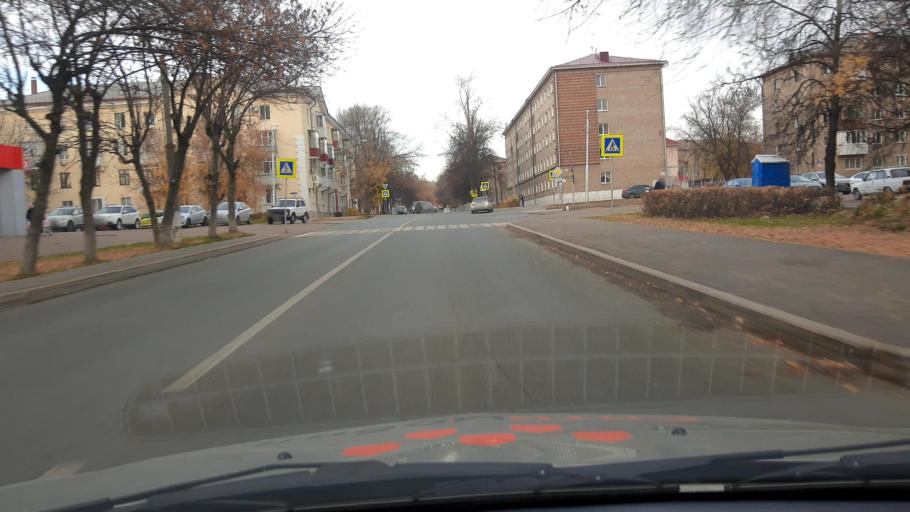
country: RU
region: Bashkortostan
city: Ufa
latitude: 54.8155
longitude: 56.0669
